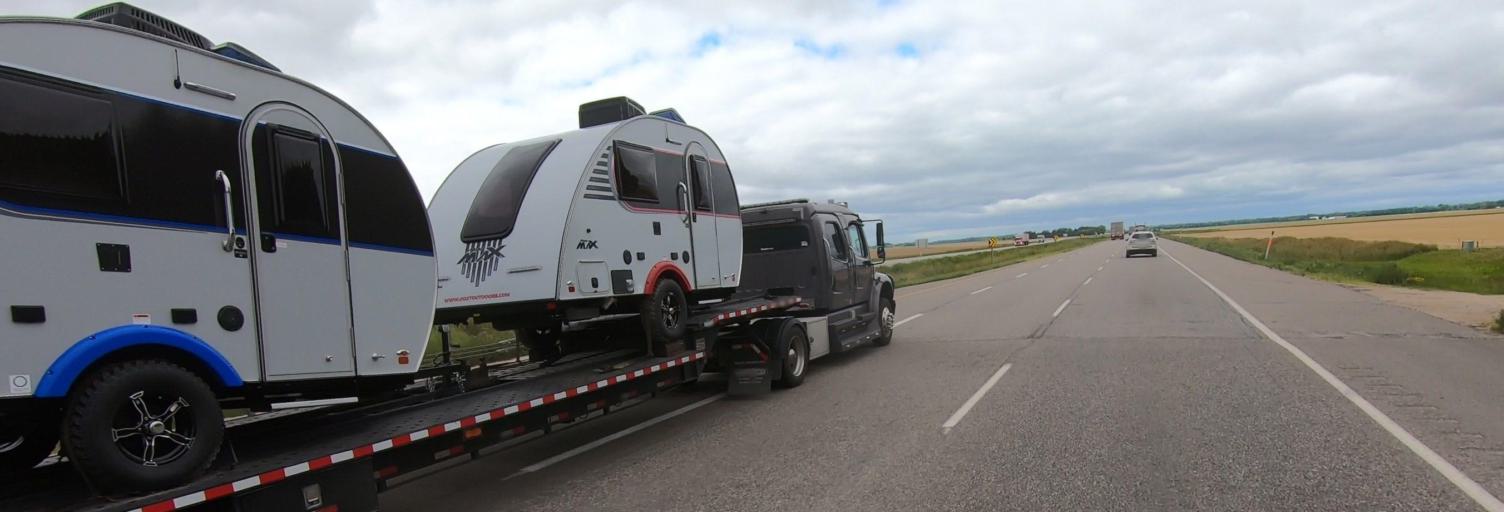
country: CA
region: Manitoba
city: Portage la Prairie
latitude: 49.9563
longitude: -98.0241
